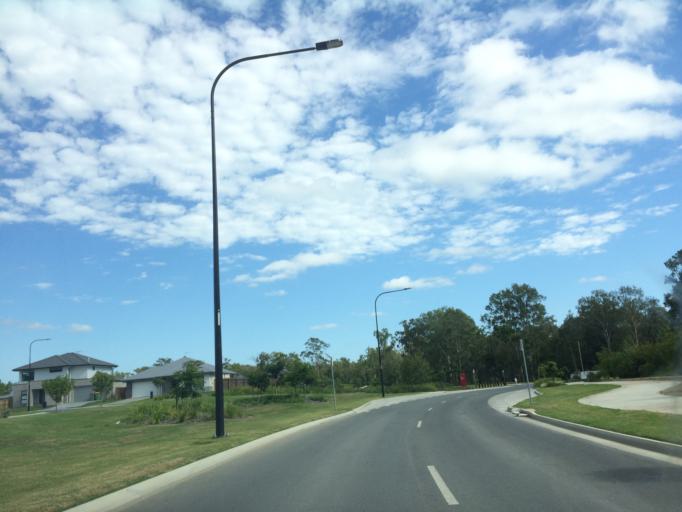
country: AU
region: Queensland
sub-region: Logan
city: North Maclean
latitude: -27.8026
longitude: 152.9455
